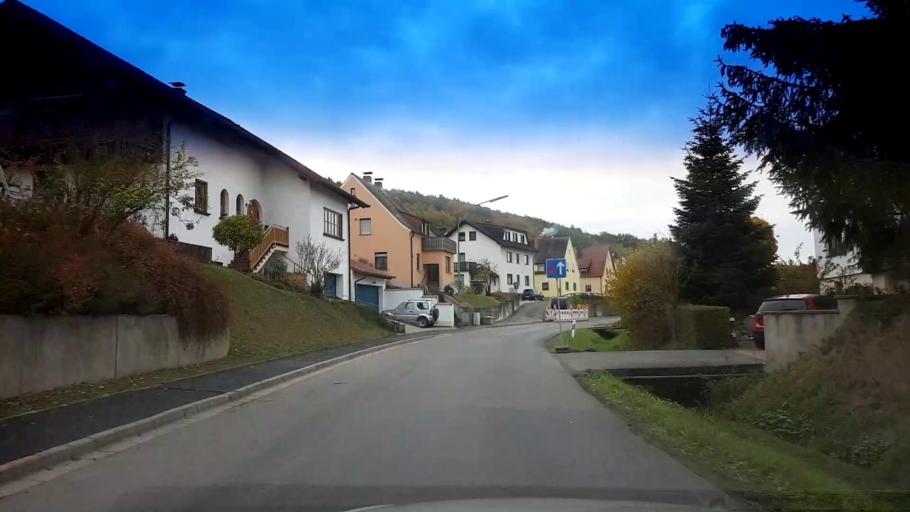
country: DE
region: Bavaria
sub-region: Upper Franconia
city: Viereth-Trunstadt
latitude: 49.9197
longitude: 10.7748
